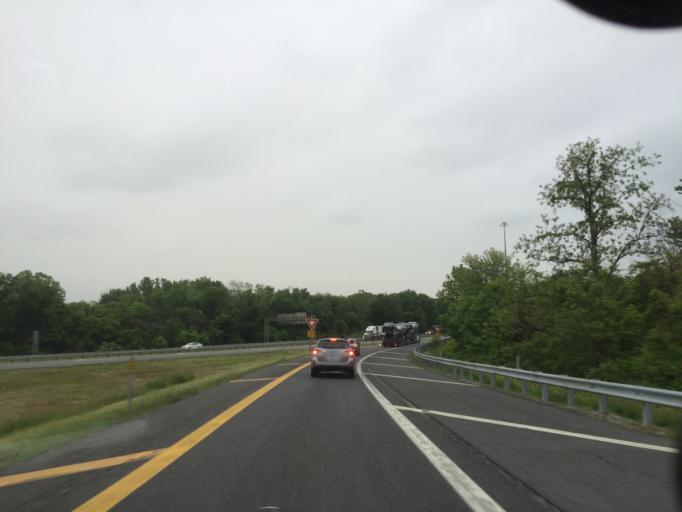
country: US
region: Maryland
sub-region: Washington County
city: Halfway
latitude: 39.6174
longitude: -77.7828
